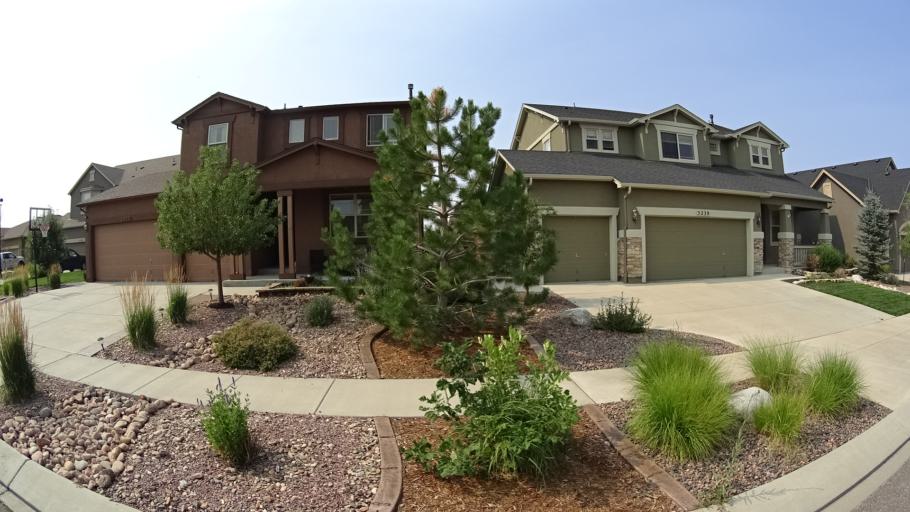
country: US
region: Colorado
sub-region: El Paso County
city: Black Forest
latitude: 38.9703
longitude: -104.7299
